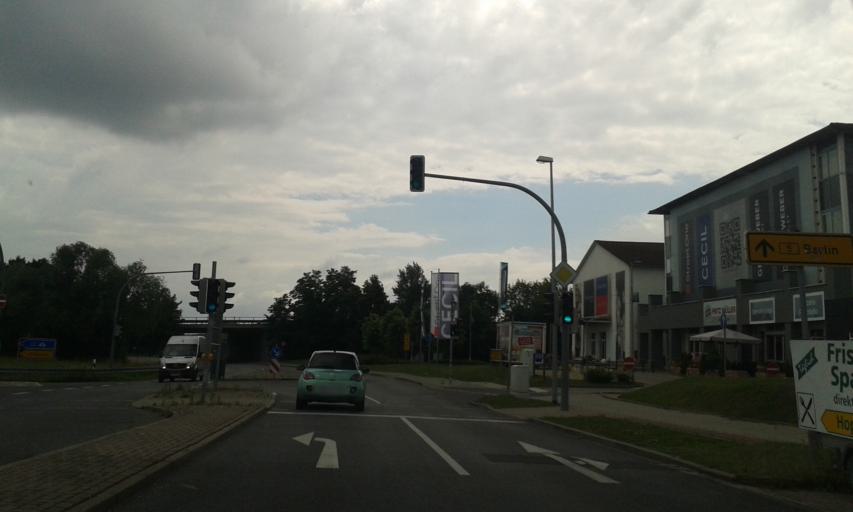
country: DE
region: Brandenburg
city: Wustermark
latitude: 52.5403
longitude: 12.9772
